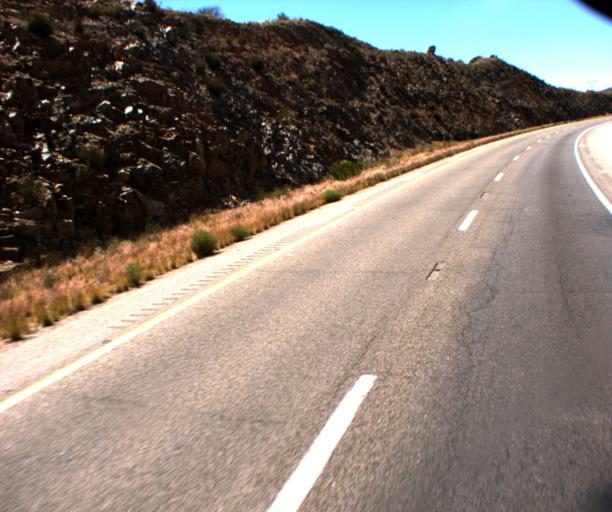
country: US
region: Arizona
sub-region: Yavapai County
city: Bagdad
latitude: 34.4583
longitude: -113.2927
